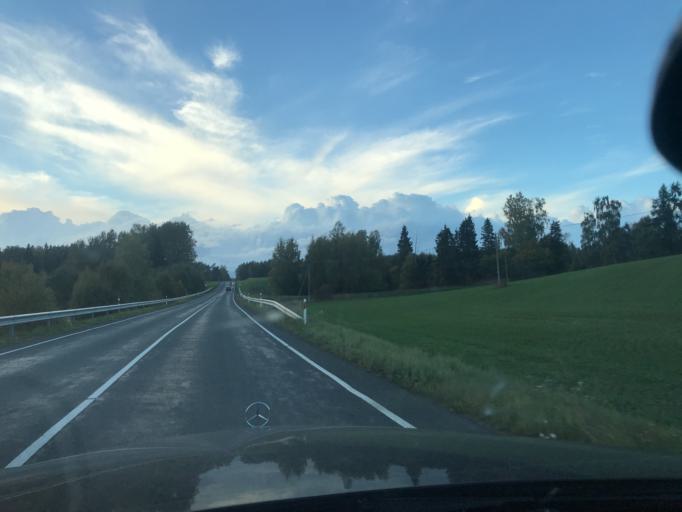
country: EE
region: Vorumaa
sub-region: Antsla vald
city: Vana-Antsla
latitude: 57.8699
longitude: 26.5986
